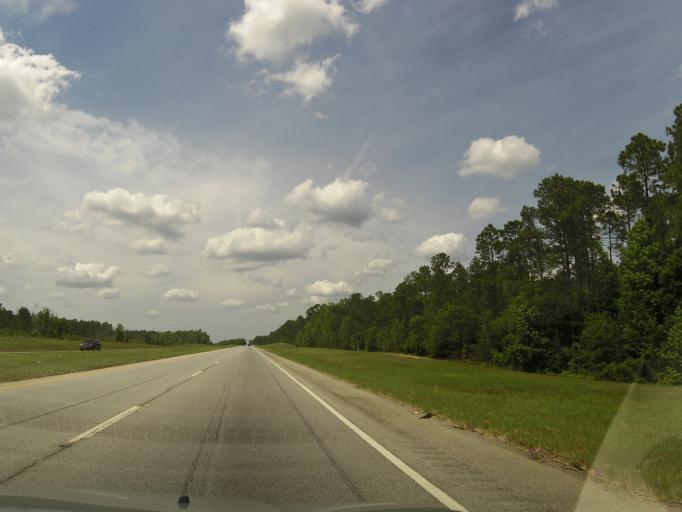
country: US
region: Georgia
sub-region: Emanuel County
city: Swainsboro
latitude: 32.6534
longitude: -82.3719
